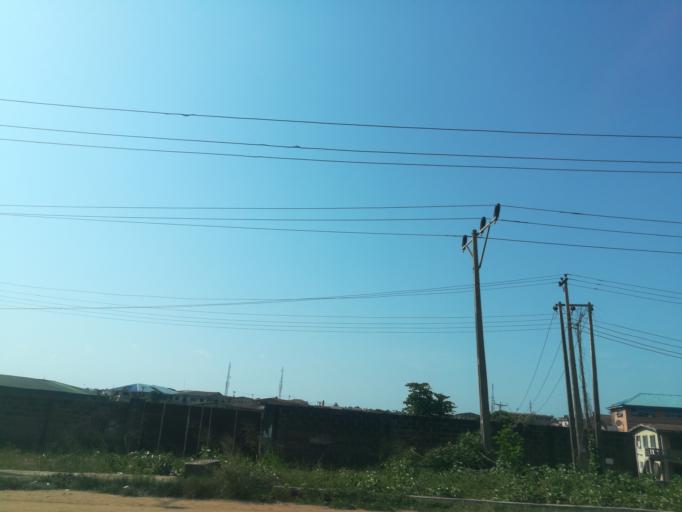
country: NG
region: Ogun
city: Abeokuta
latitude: 7.1417
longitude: 3.3139
